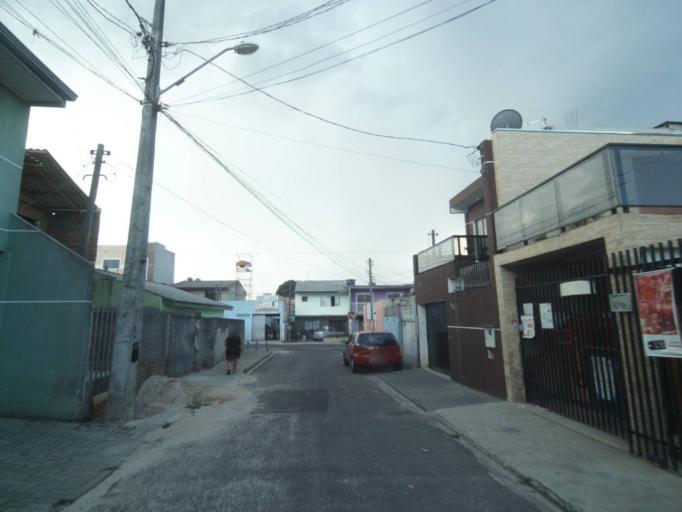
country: BR
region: Parana
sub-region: Sao Jose Dos Pinhais
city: Sao Jose dos Pinhais
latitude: -25.5326
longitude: -49.2734
